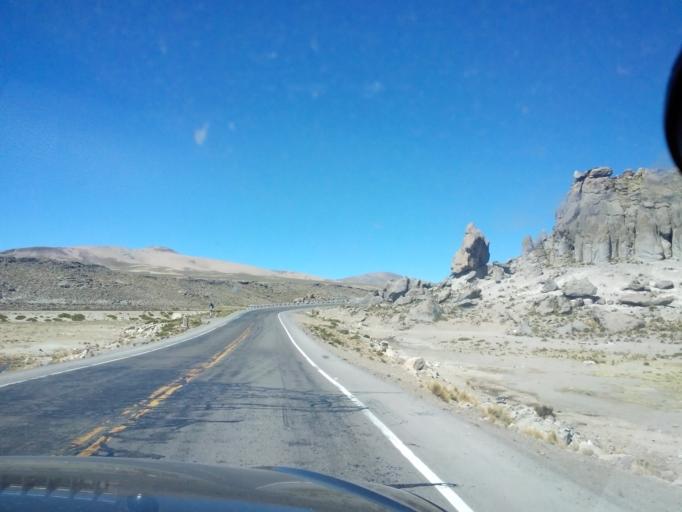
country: PE
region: Arequipa
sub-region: Provincia de Caylloma
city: Vizcachane
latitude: -15.9284
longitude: -71.1909
